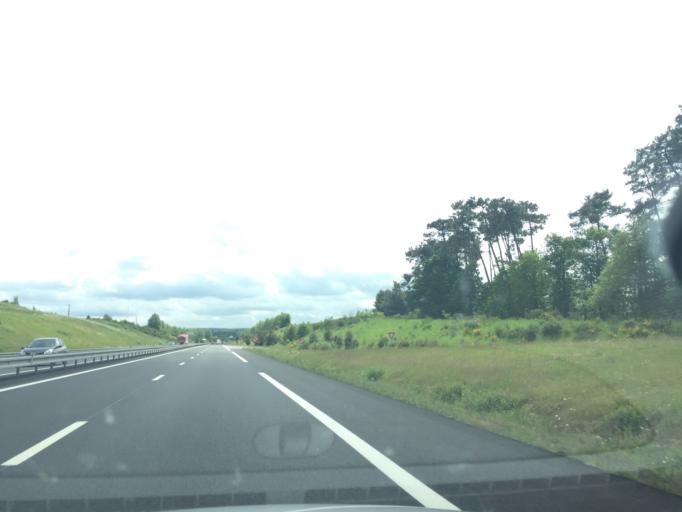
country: FR
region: Pays de la Loire
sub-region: Departement de la Sarthe
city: Ecommoy
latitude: 47.8210
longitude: 0.3068
